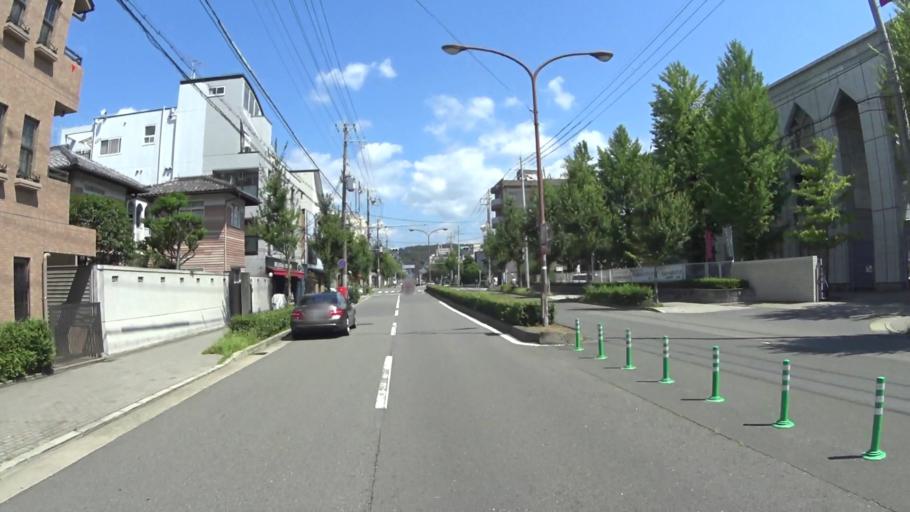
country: JP
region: Kyoto
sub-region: Kyoto-shi
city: Kamigyo-ku
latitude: 35.0459
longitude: 135.7706
